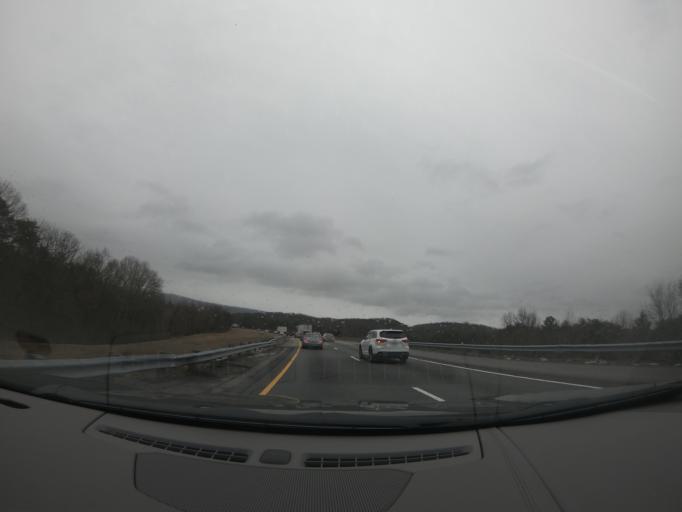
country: US
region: Georgia
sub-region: Walker County
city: Lookout Mountain
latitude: 34.9720
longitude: -85.4523
